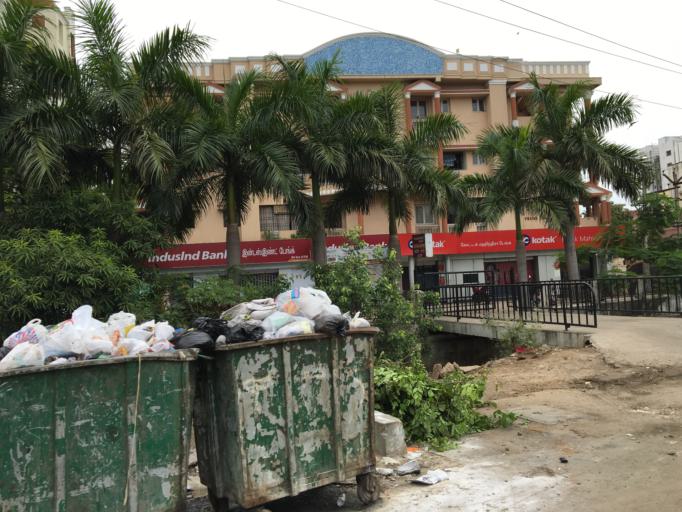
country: IN
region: Tamil Nadu
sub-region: Kancheepuram
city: Alandur
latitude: 12.9806
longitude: 80.2182
